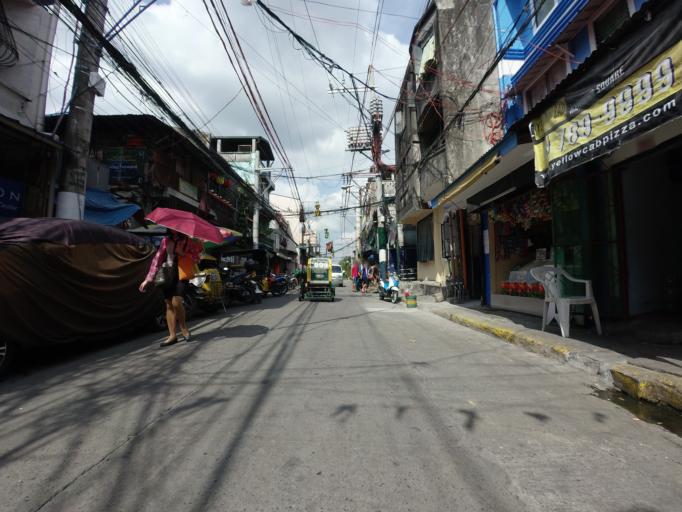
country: PH
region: Metro Manila
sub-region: City of Manila
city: Quiapo
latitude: 14.5728
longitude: 120.9962
